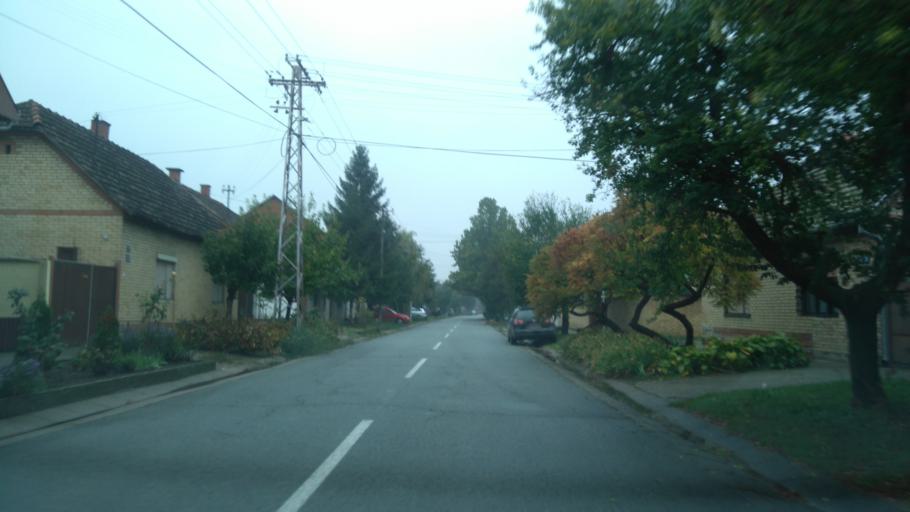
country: RS
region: Autonomna Pokrajina Vojvodina
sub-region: Juznobacki Okrug
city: Becej
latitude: 45.6200
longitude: 20.0594
